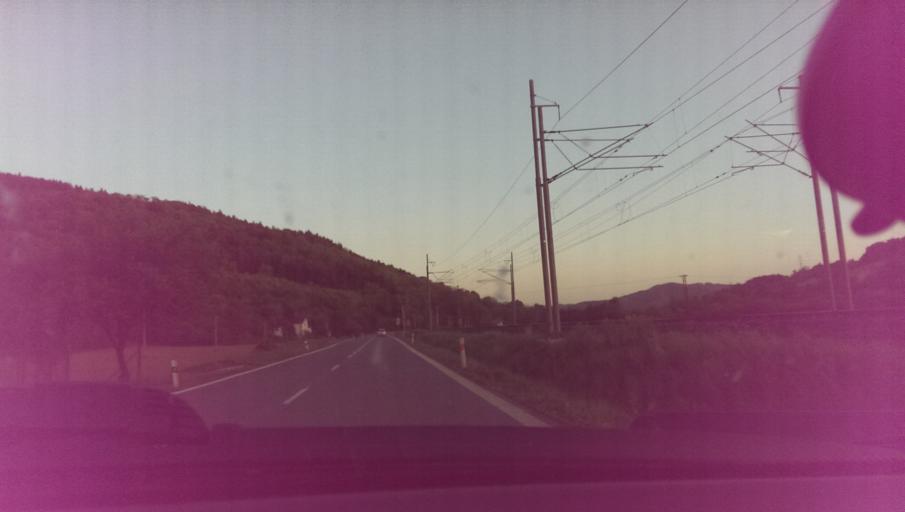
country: CZ
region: Zlin
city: Jablunka
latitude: 49.4099
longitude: 17.9531
